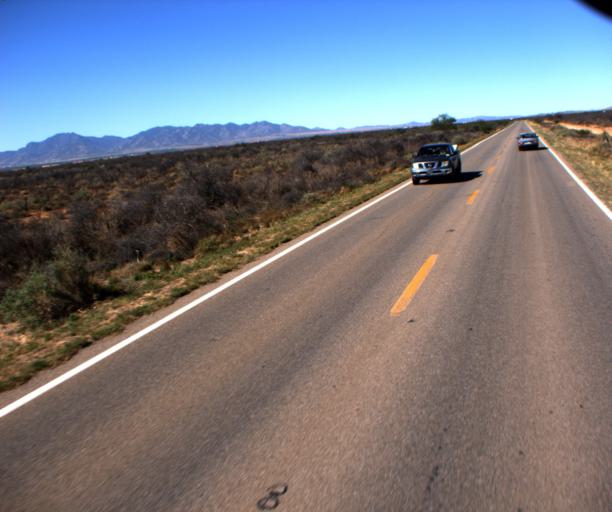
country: US
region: Arizona
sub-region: Cochise County
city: Huachuca City
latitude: 31.6998
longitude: -110.2988
